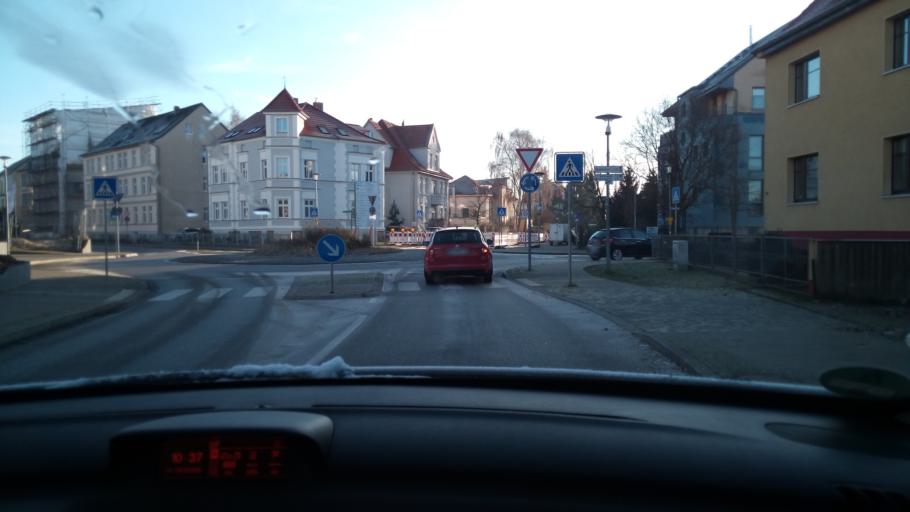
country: DE
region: Mecklenburg-Vorpommern
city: Neubrandenburg
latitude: 53.5610
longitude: 13.2486
